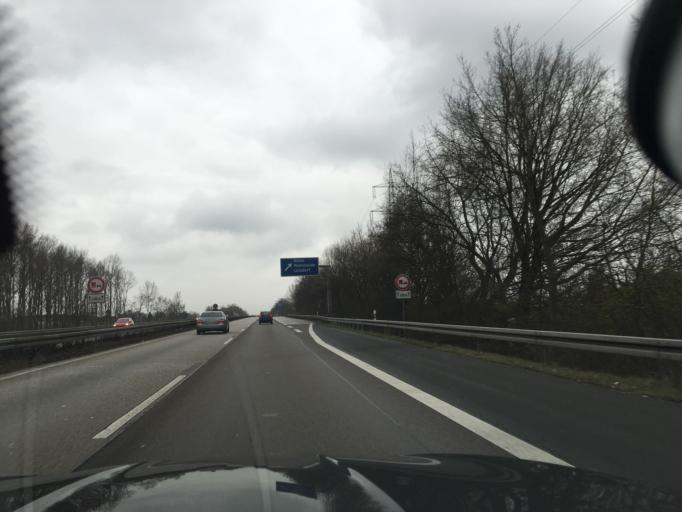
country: DE
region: North Rhine-Westphalia
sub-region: Regierungsbezirk Koln
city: Wahn-Heide
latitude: 50.8631
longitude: 7.0961
